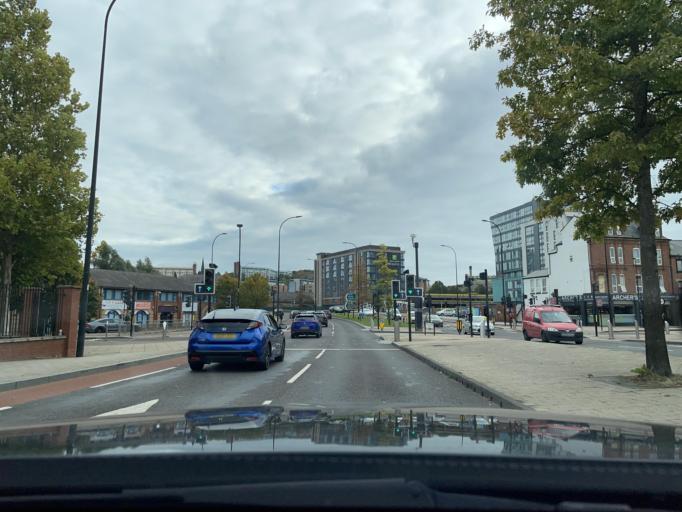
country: GB
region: England
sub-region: Sheffield
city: Sheffield
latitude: 53.3878
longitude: -1.4624
